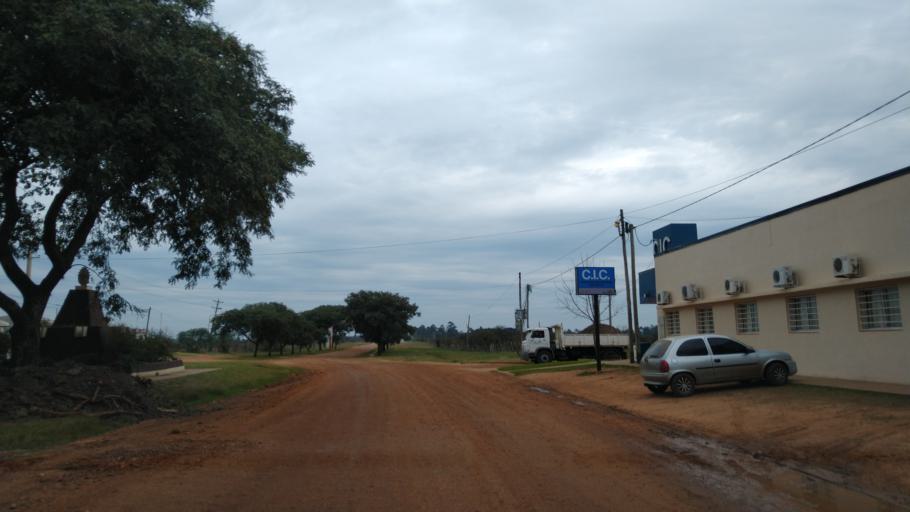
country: AR
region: Entre Rios
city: Villa del Rosario
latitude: -30.7948
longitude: -57.9181
